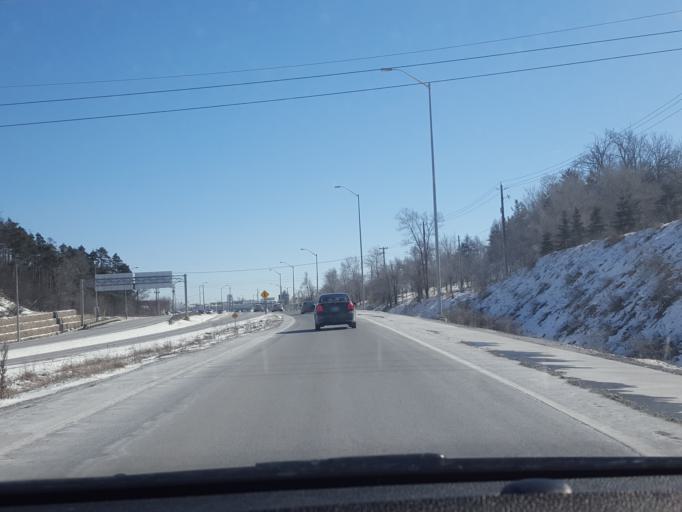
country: CA
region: Ontario
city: Kitchener
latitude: 43.4139
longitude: -80.4051
